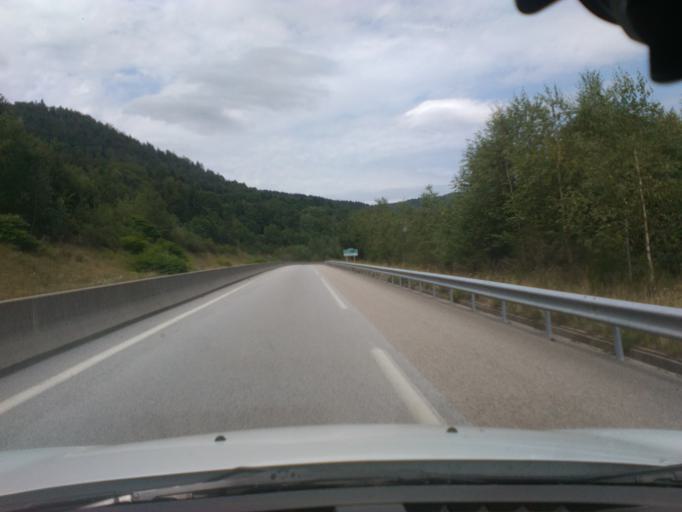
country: FR
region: Lorraine
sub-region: Departement des Vosges
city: Rupt-sur-Moselle
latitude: 47.9389
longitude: 6.6357
